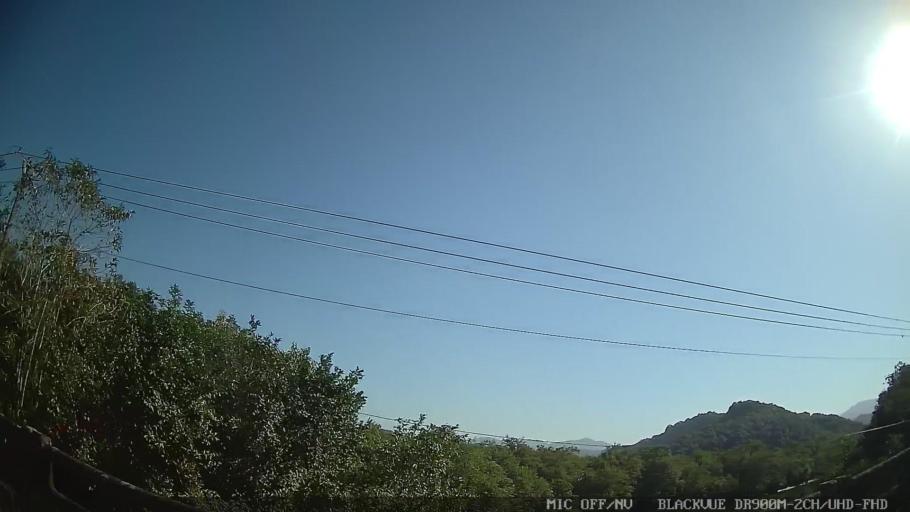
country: BR
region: Sao Paulo
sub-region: Santos
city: Santos
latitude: -23.9076
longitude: -46.3129
